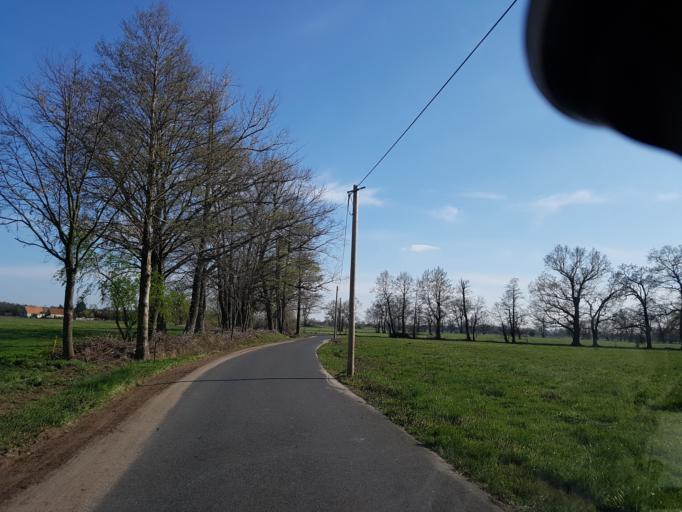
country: DE
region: Brandenburg
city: Schilda
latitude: 51.6312
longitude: 13.3104
